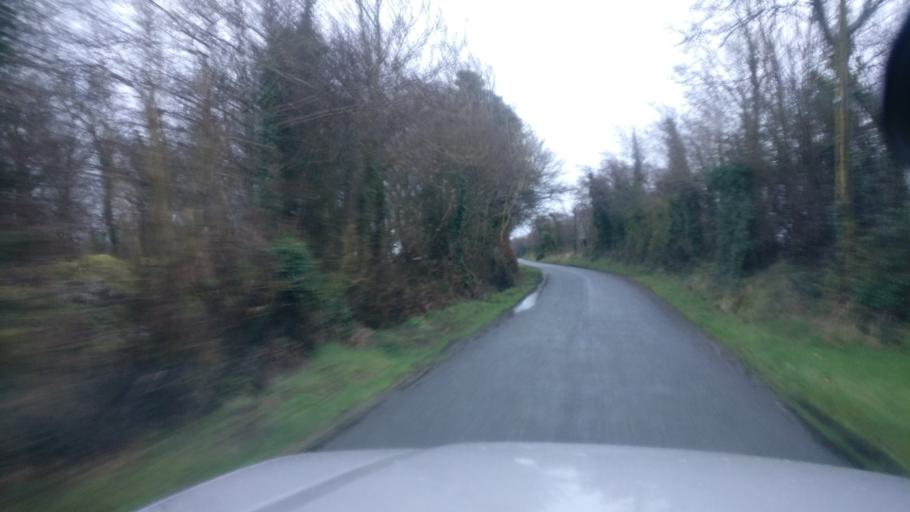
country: IE
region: Connaught
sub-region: County Galway
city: Ballinasloe
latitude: 53.3227
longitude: -8.3834
